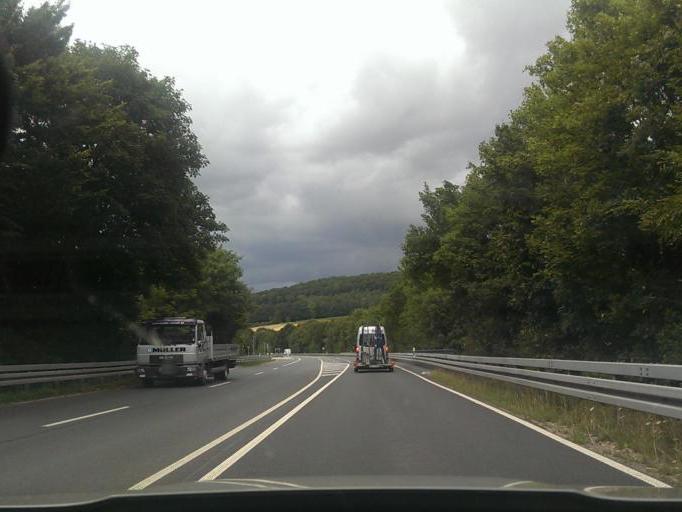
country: DE
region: North Rhine-Westphalia
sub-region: Regierungsbezirk Detmold
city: Schieder-Schwalenberg
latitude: 51.8495
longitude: 9.1489
